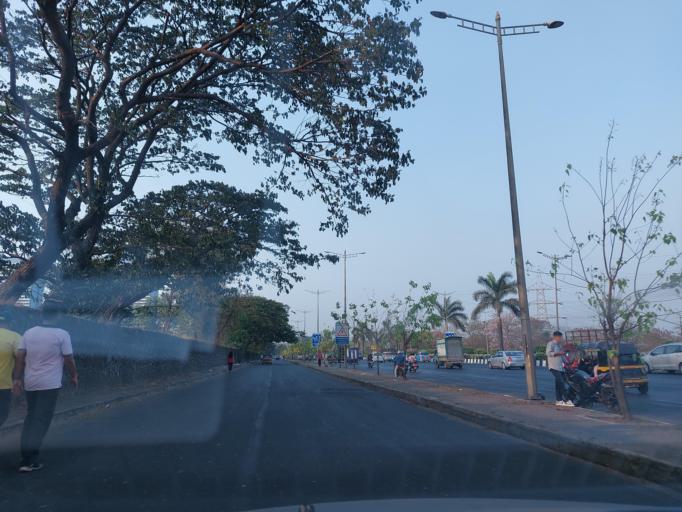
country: IN
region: Maharashtra
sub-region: Mumbai Suburban
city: Powai
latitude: 19.0979
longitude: 72.9275
